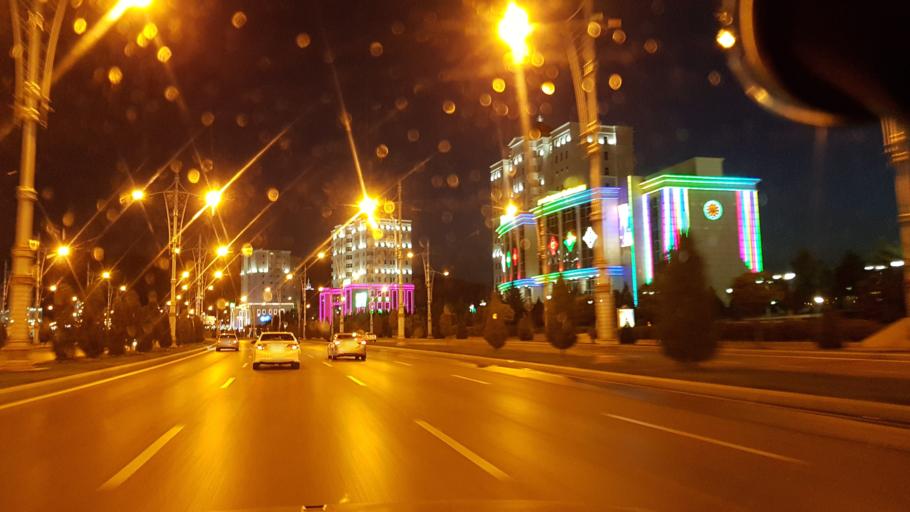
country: TM
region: Ahal
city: Ashgabat
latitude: 37.9170
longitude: 58.3475
